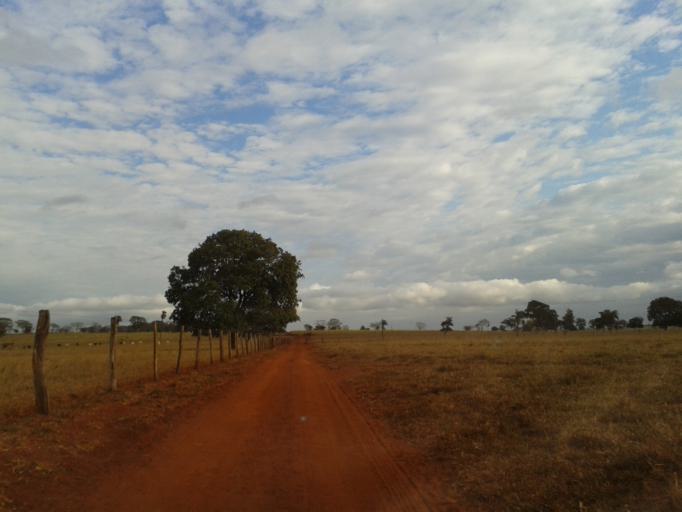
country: BR
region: Minas Gerais
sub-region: Santa Vitoria
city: Santa Vitoria
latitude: -18.7397
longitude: -50.2168
